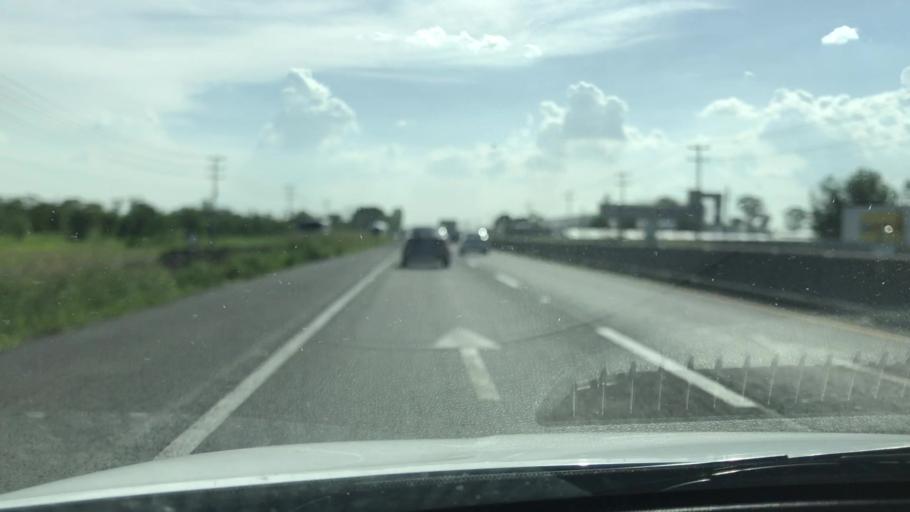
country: MX
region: Guanajuato
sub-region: Celaya
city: Colonia Fraccionamiento el Puente
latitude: 20.5144
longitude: -100.9044
